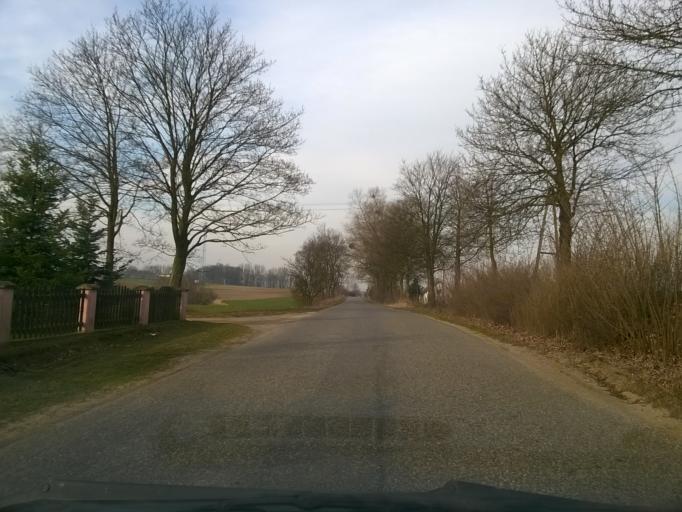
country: PL
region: Kujawsko-Pomorskie
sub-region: Powiat tucholski
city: Kesowo
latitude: 53.5479
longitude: 17.6800
